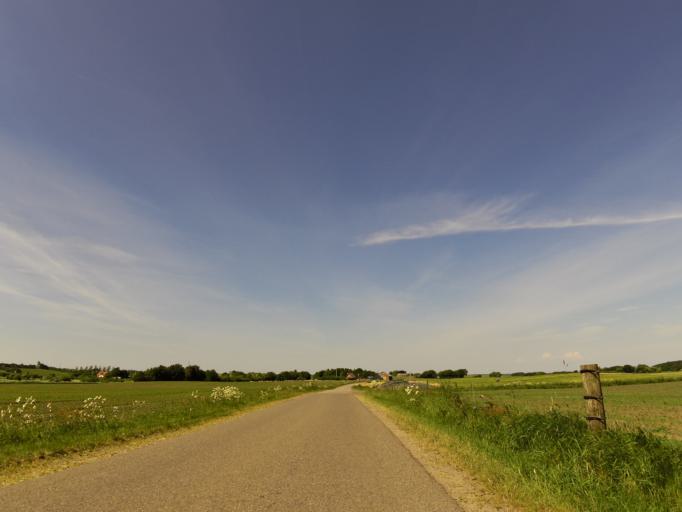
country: DK
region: Central Jutland
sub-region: Holstebro Kommune
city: Vinderup
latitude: 56.4359
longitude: 8.8710
